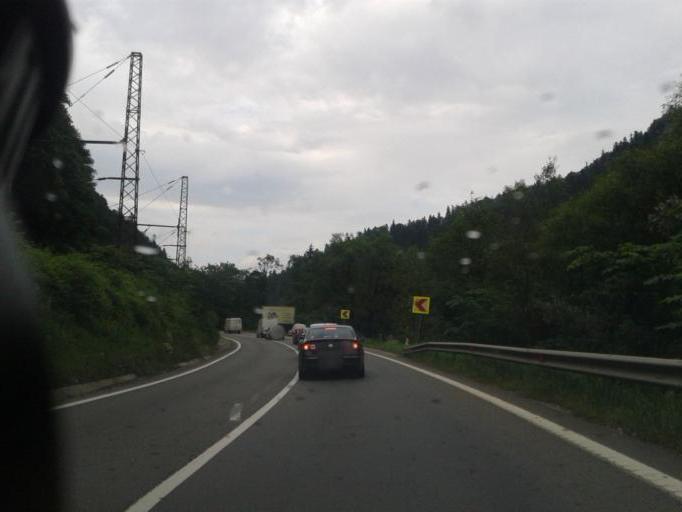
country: RO
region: Brasov
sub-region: Oras Predeal
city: Predeal
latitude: 45.5631
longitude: 25.6024
